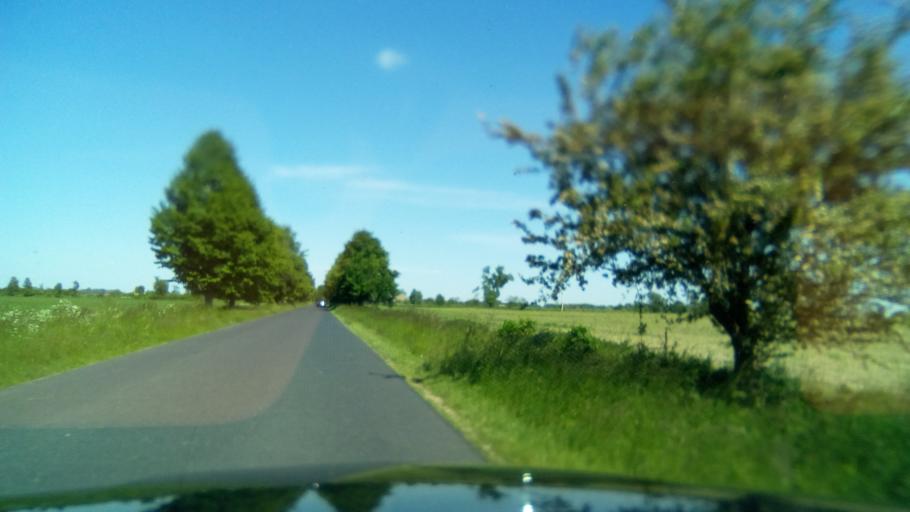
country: PL
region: Greater Poland Voivodeship
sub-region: Powiat gnieznienski
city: Niechanowo
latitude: 52.4561
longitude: 17.6357
